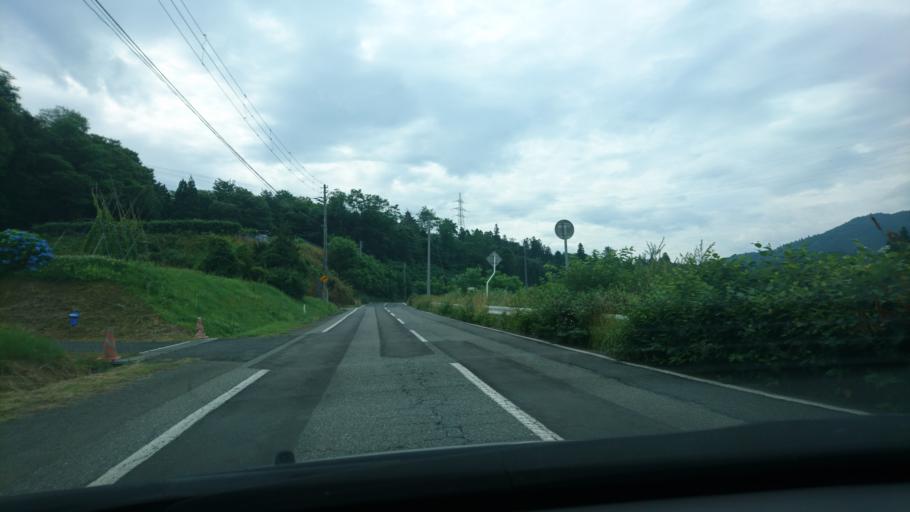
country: JP
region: Iwate
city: Ichinoseki
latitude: 38.8954
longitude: 141.4252
